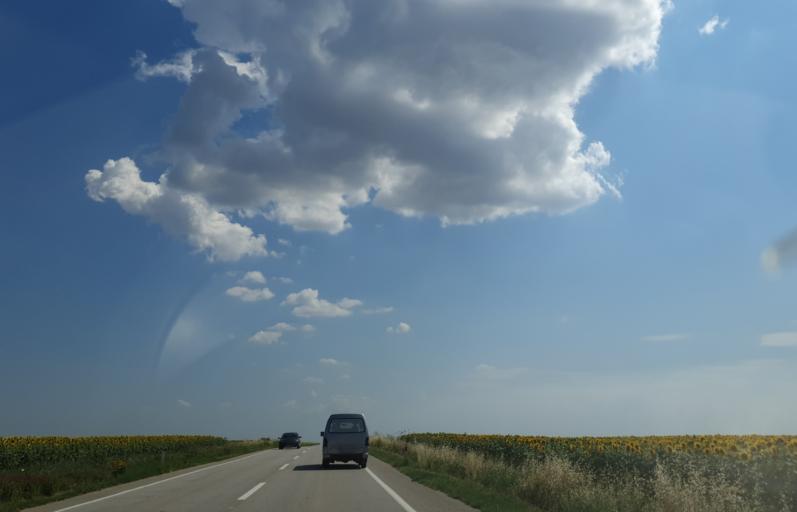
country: TR
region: Kirklareli
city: Buyukkaristiran
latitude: 41.4069
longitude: 27.5760
